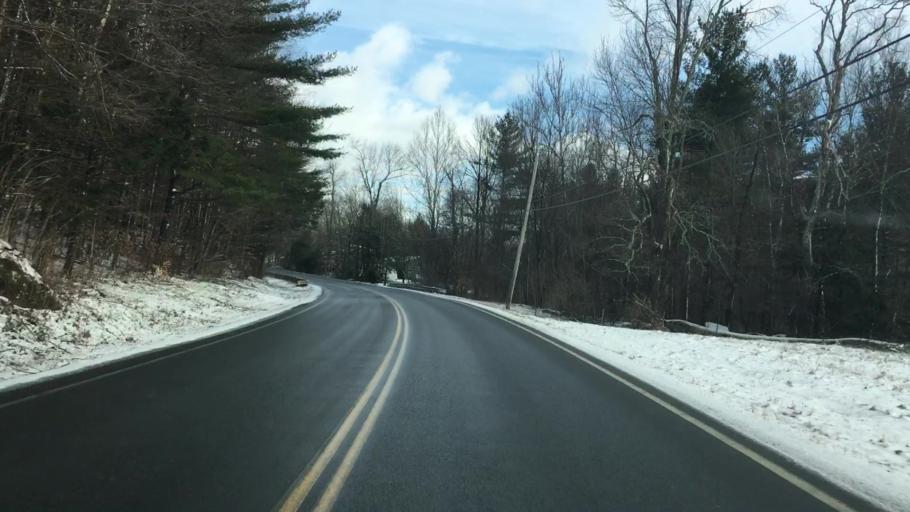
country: US
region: Massachusetts
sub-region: Franklin County
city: Colrain
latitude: 42.7024
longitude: -72.6969
